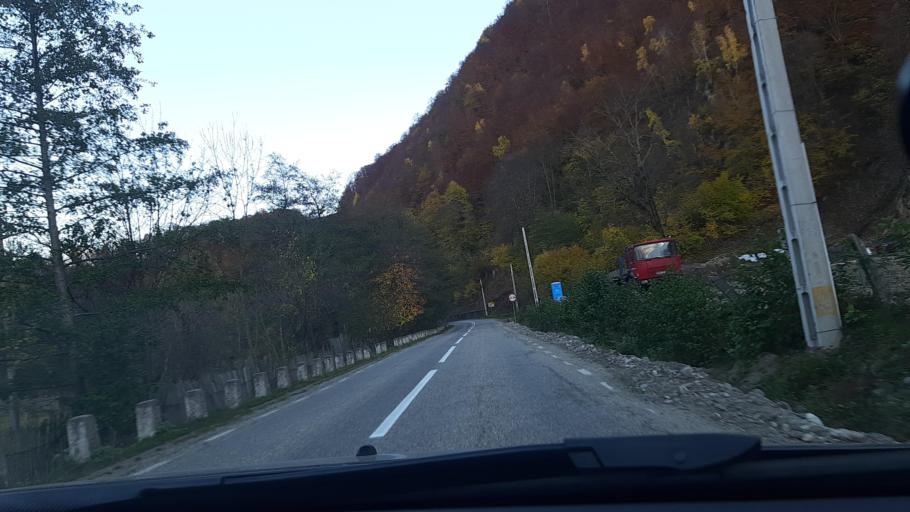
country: RO
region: Valcea
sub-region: Comuna Brezoi
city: Brezoi
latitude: 45.3480
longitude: 24.1447
